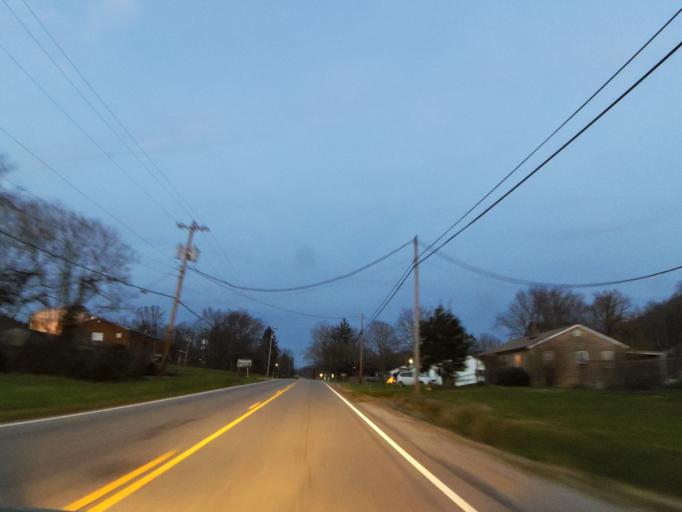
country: US
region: Tennessee
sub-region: Morgan County
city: Coalfield
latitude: 36.0165
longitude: -84.3785
